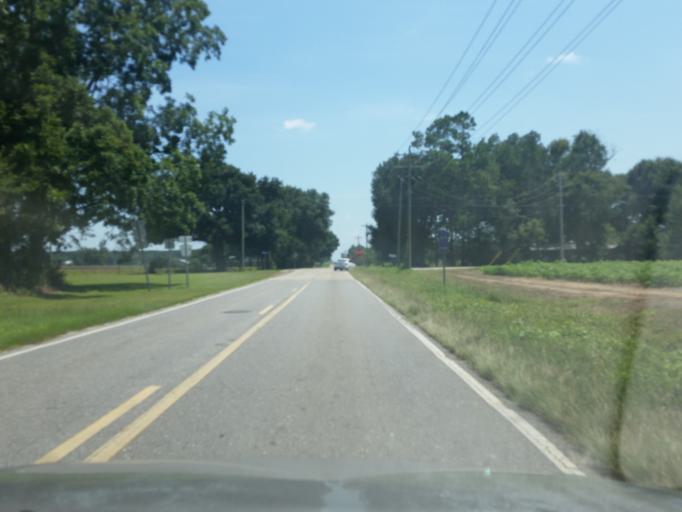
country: US
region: Alabama
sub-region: Baldwin County
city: Robertsdale
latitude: 30.6196
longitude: -87.6661
